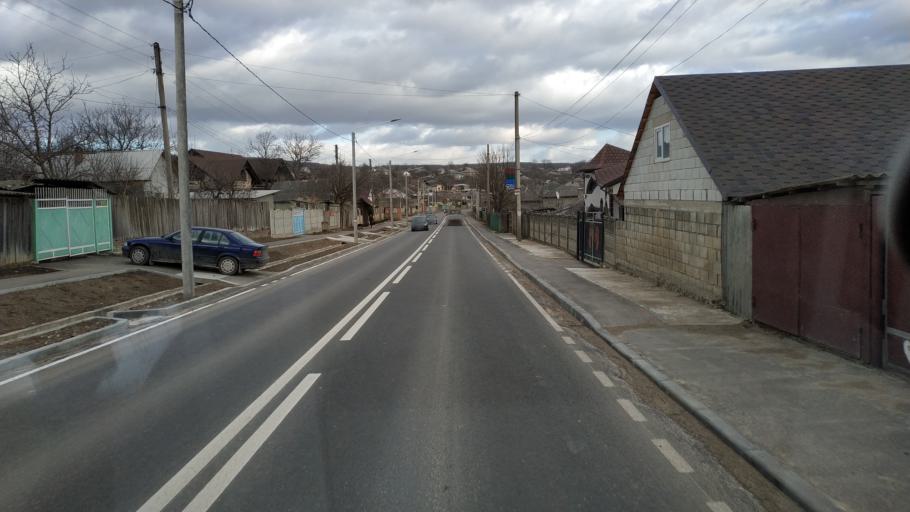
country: MD
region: Calarasi
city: Calarasi
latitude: 47.2897
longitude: 28.1897
